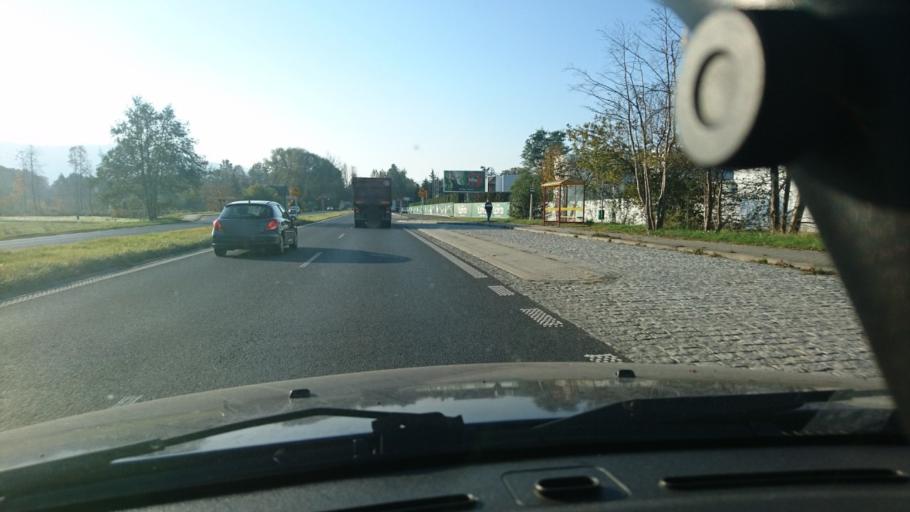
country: PL
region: Silesian Voivodeship
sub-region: Powiat cieszynski
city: Gorki Wielkie
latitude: 49.7708
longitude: 18.8084
